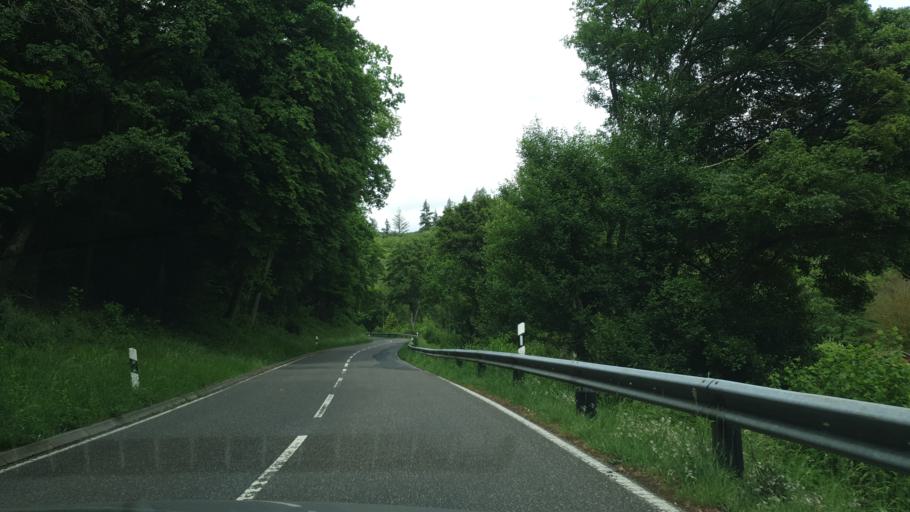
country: DE
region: Rheinland-Pfalz
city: Seelbach
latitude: 50.3401
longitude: 7.8592
